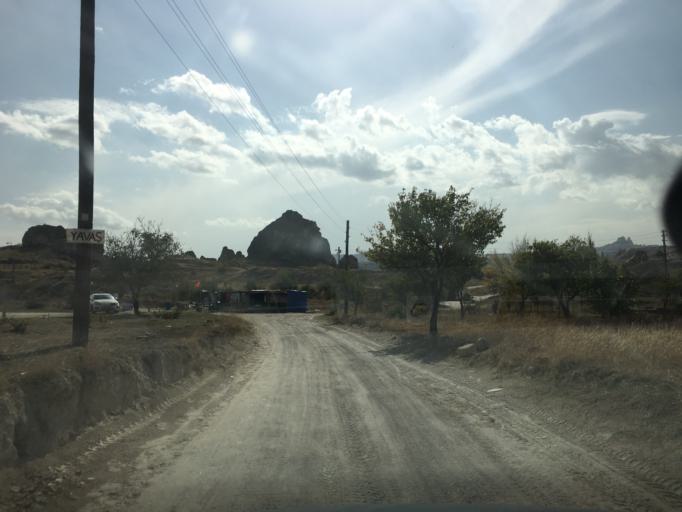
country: TR
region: Nevsehir
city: Goereme
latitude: 38.6629
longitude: 34.8412
